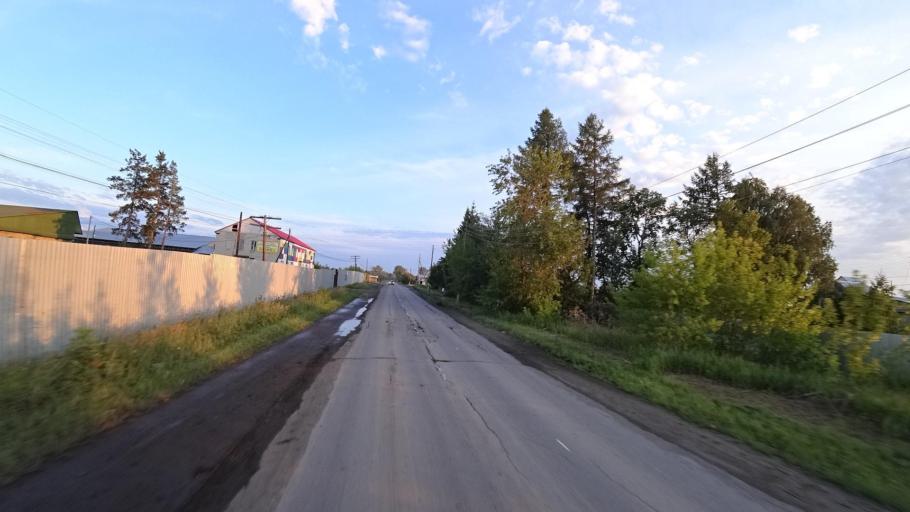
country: RU
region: Sverdlovsk
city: Kamyshlov
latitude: 56.8651
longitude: 62.7102
